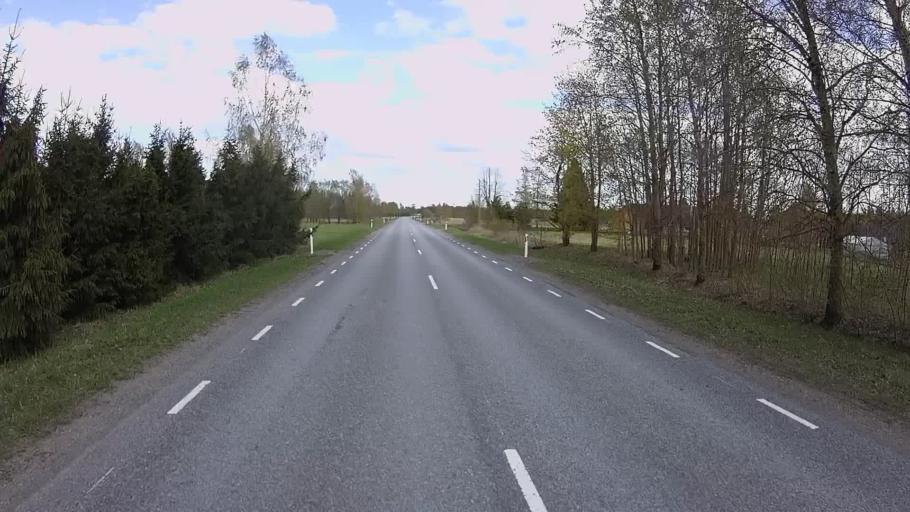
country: EE
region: Jogevamaa
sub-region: Mustvee linn
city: Mustvee
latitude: 58.7866
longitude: 26.9637
